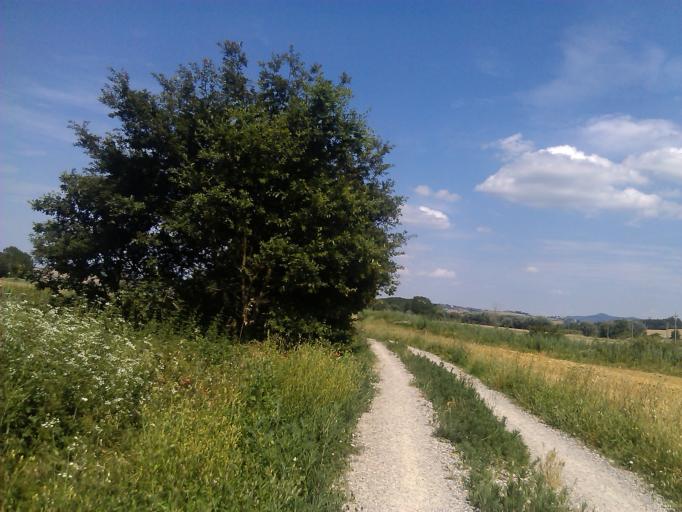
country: IT
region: Tuscany
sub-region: Provincia di Siena
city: Chiusi
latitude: 43.0526
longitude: 11.9410
